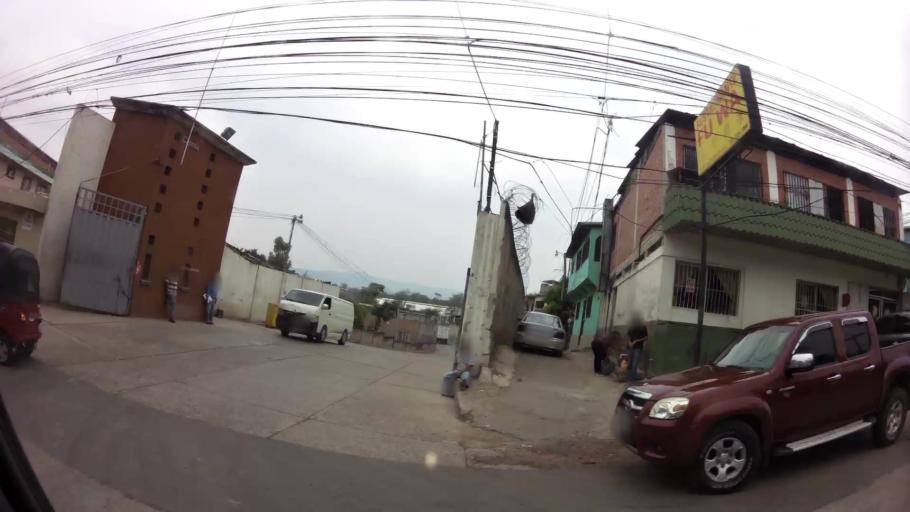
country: HN
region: Francisco Morazan
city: Tegucigalpa
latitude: 14.0674
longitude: -87.2126
